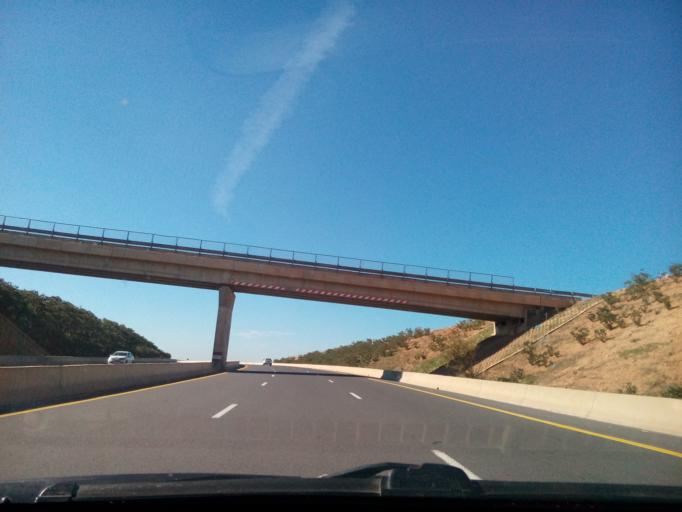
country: DZ
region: Tlemcen
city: Chetouane
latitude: 34.9606
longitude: -1.2911
